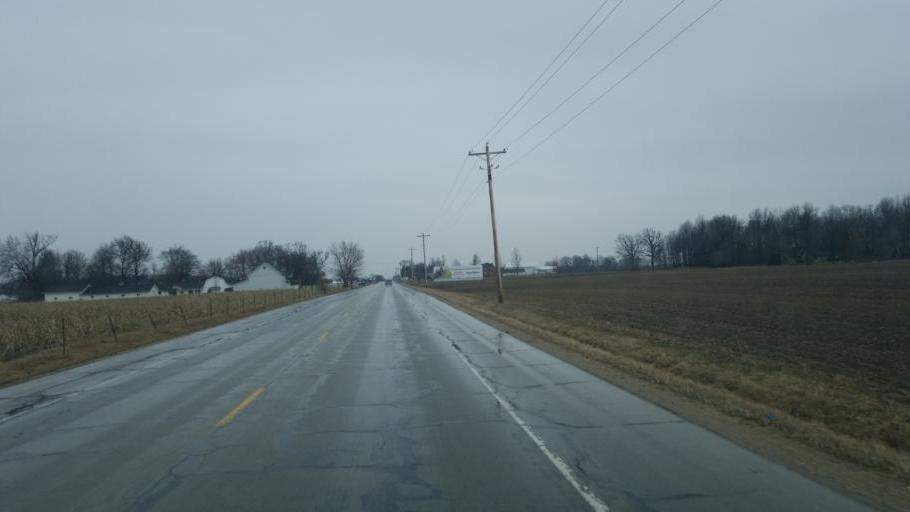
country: US
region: Indiana
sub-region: Adams County
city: Berne
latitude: 40.6997
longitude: -84.9559
